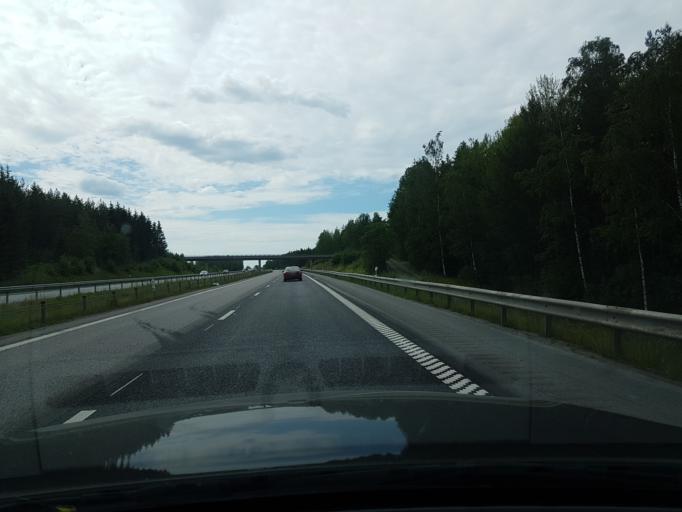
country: SE
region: Stockholm
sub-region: Norrtalje Kommun
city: Norrtalje
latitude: 59.7429
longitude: 18.6481
